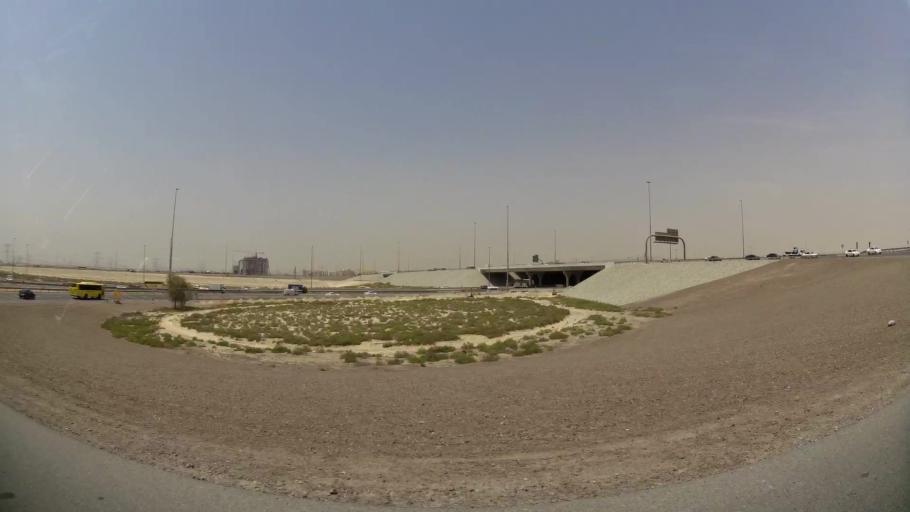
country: AE
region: Ash Shariqah
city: Sharjah
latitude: 25.1788
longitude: 55.3950
